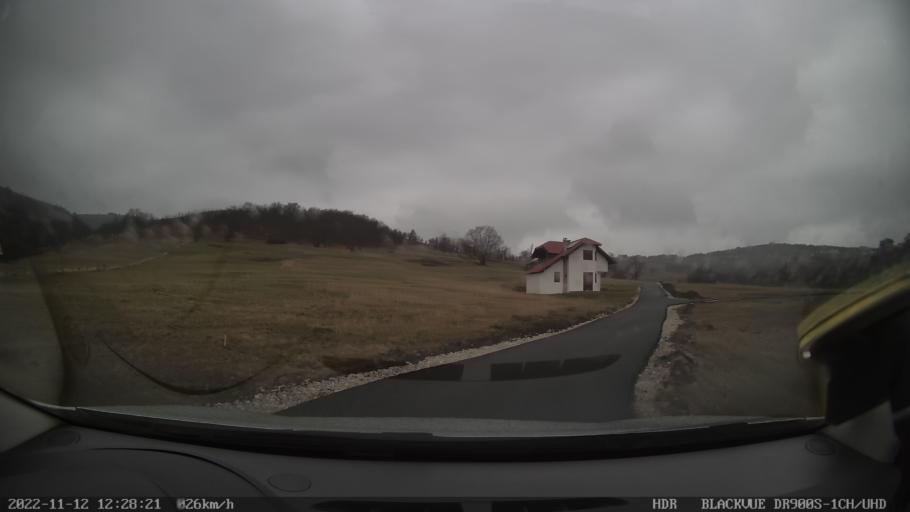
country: RS
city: Zlatibor
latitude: 43.7040
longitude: 19.7191
